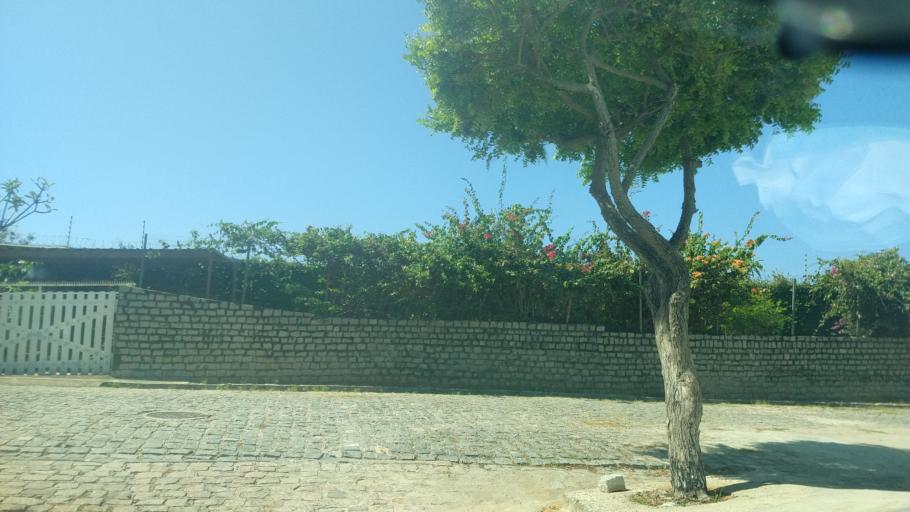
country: BR
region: Rio Grande do Norte
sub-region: Parnamirim
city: Parnamirim
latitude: -5.9472
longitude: -35.1542
